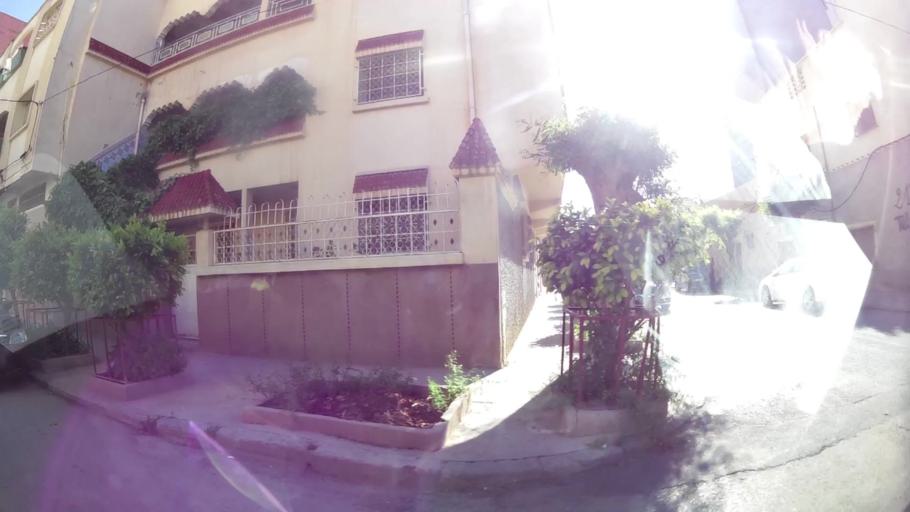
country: MA
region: Oriental
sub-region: Oujda-Angad
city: Oujda
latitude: 34.6891
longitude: -1.9186
